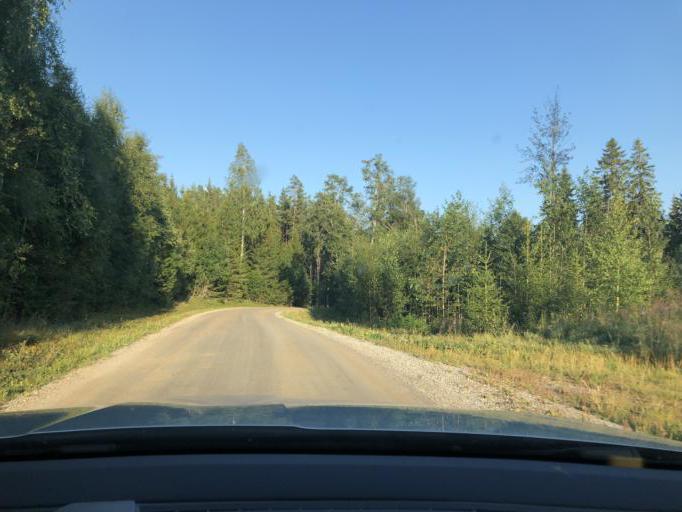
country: SE
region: Vaesternorrland
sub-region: Kramfors Kommun
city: Bollstabruk
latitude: 63.0533
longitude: 17.7107
